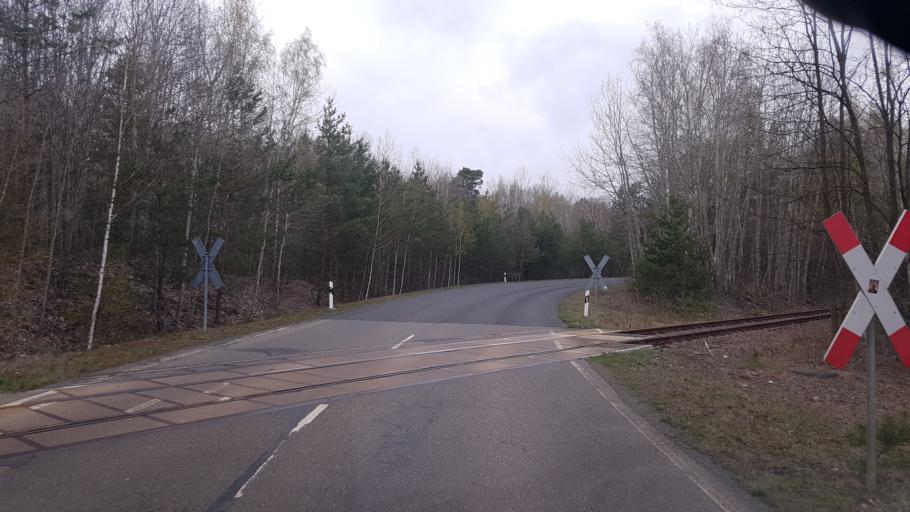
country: DE
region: Brandenburg
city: Lauchhammer
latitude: 51.4854
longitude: 13.7893
